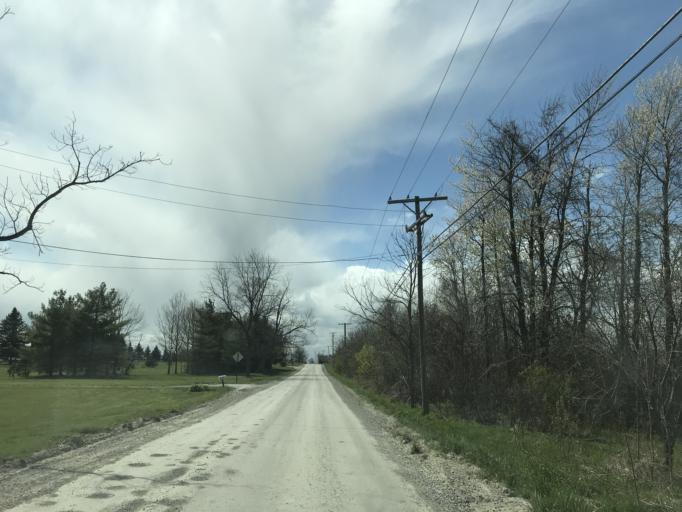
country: US
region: Michigan
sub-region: Oakland County
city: South Lyon
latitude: 42.3879
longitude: -83.6465
